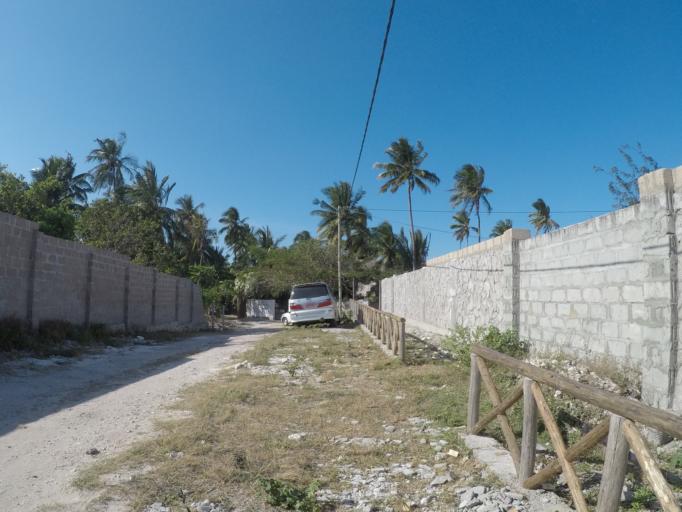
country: TZ
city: Kiwengwa
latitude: -6.1538
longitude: 39.5185
